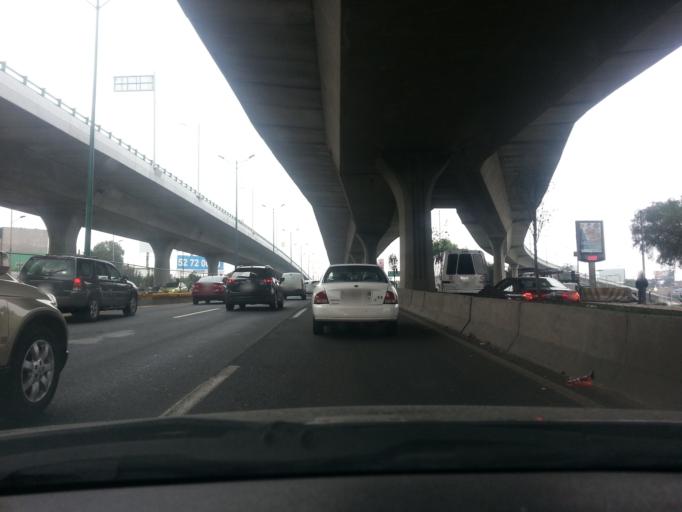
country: MX
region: Mexico
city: Naucalpan de Juarez
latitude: 19.4786
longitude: -99.2313
